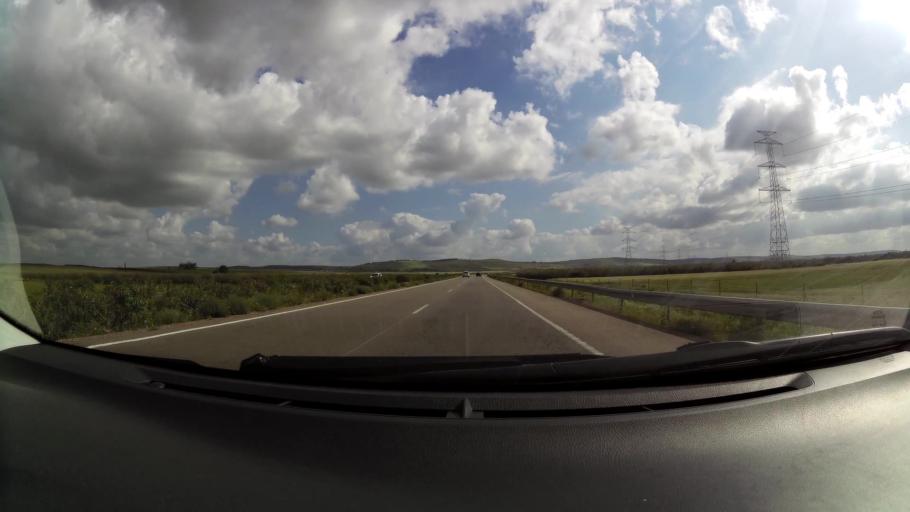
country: MA
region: Chaouia-Ouardigha
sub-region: Settat Province
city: Settat
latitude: 33.1070
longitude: -7.5825
